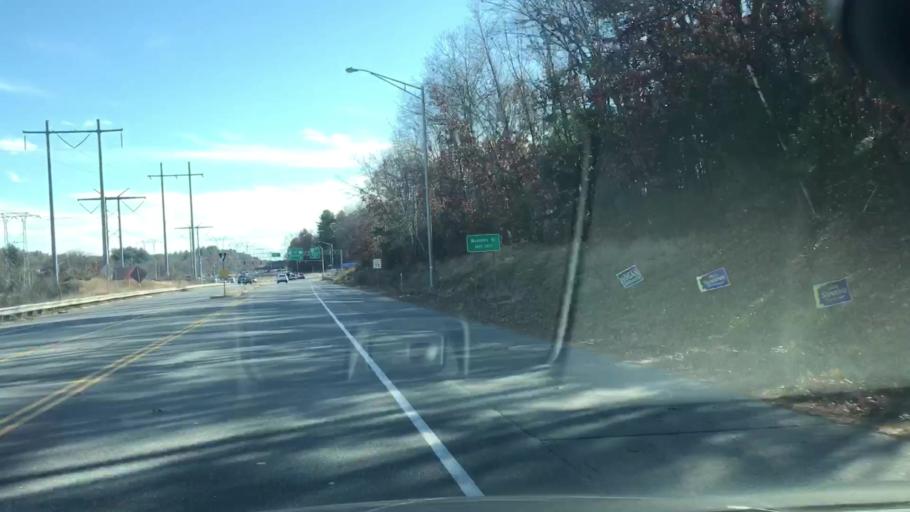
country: US
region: New Hampshire
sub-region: Hillsborough County
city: Bedford
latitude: 42.9626
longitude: -71.5037
